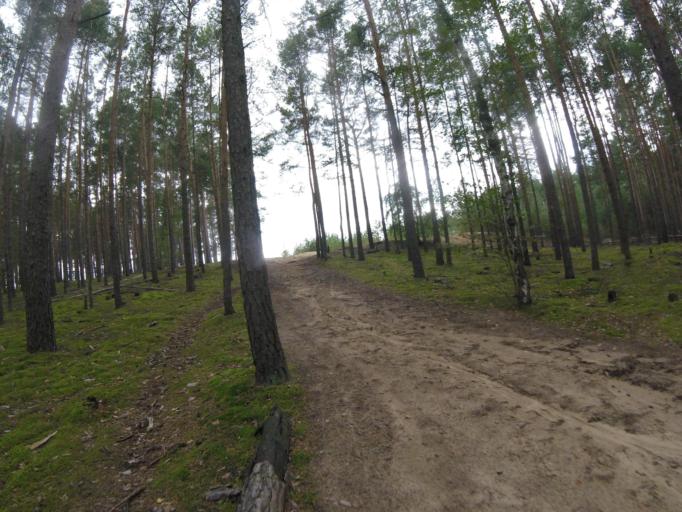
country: DE
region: Brandenburg
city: Gross Koris
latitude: 52.2068
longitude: 13.6582
